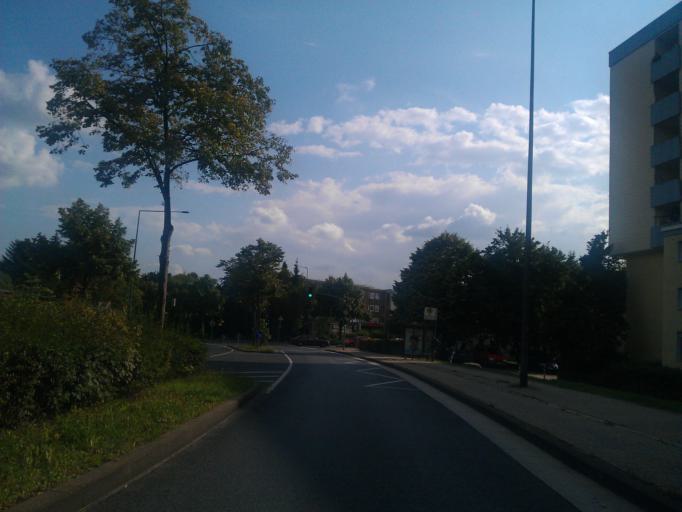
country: DE
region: North Rhine-Westphalia
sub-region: Regierungsbezirk Koln
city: Aachen
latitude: 50.7751
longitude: 6.0575
